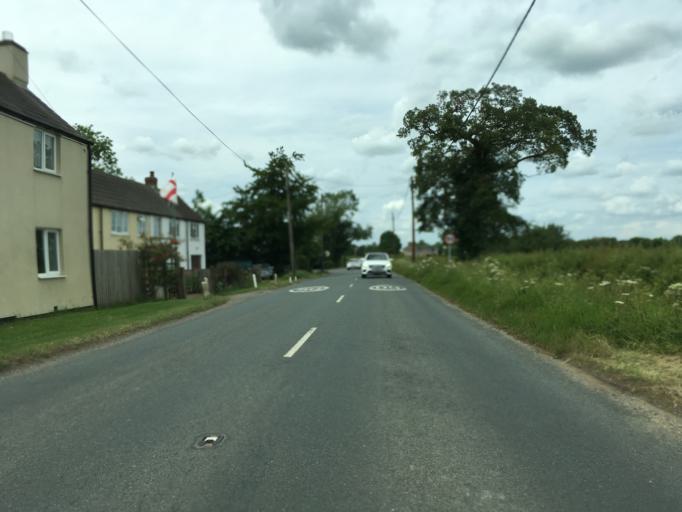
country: GB
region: England
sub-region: Wiltshire
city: Lyneham
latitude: 51.5638
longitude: -1.9540
